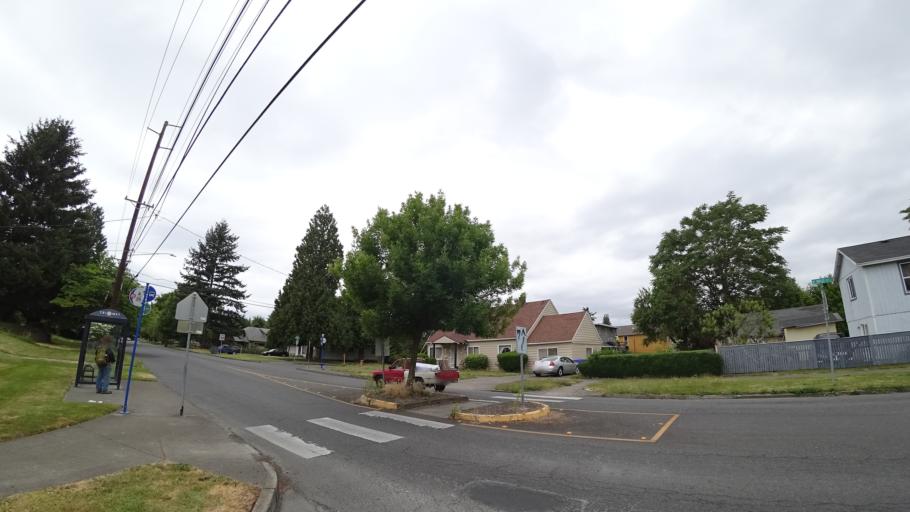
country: US
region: Oregon
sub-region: Multnomah County
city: Portland
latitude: 45.5839
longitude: -122.6999
